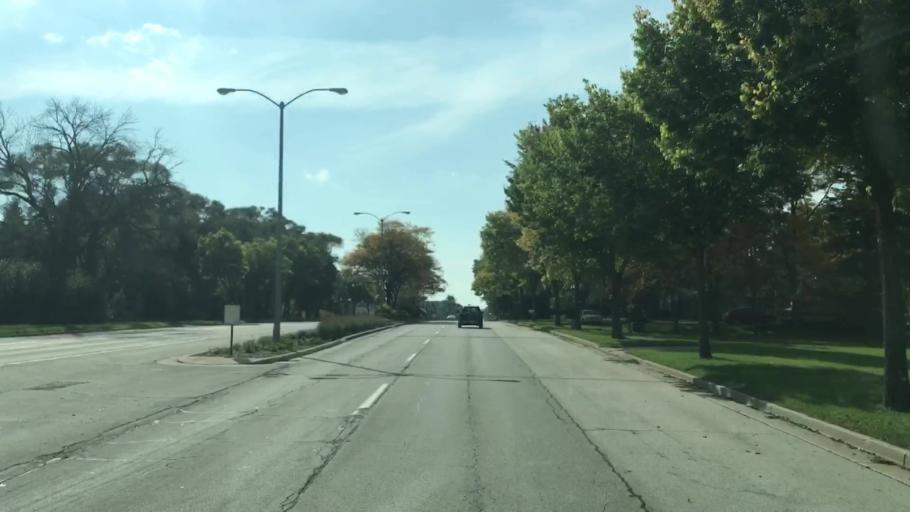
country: US
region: Wisconsin
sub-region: Waukesha County
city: Butler
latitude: 43.1653
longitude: -88.0445
